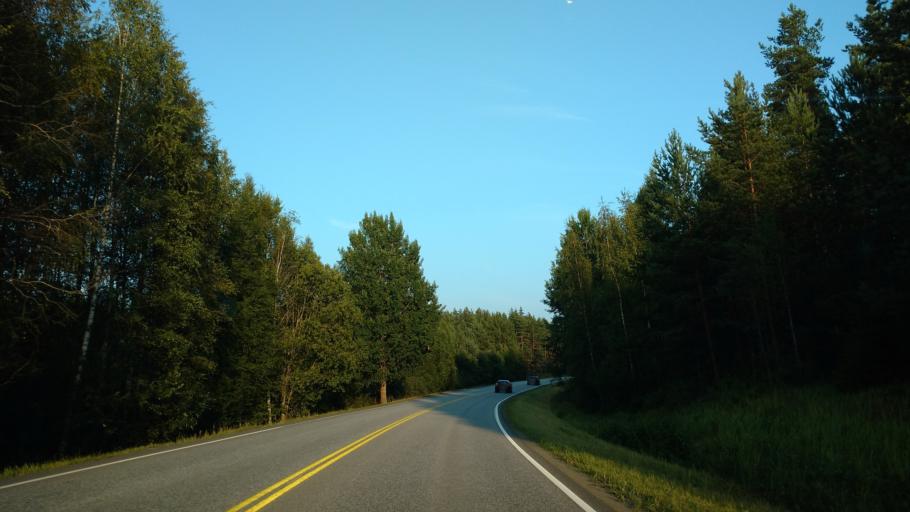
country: FI
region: Varsinais-Suomi
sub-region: Salo
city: Saerkisalo
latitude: 60.1784
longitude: 22.9487
